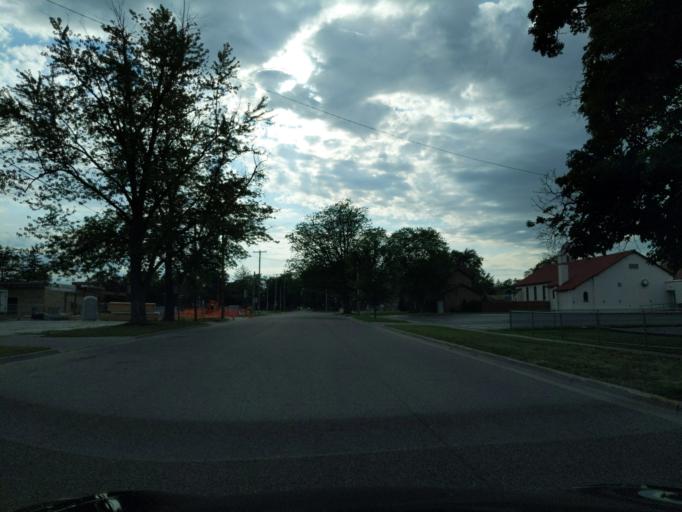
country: US
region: Michigan
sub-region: Clare County
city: Clare
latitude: 43.8224
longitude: -84.7666
